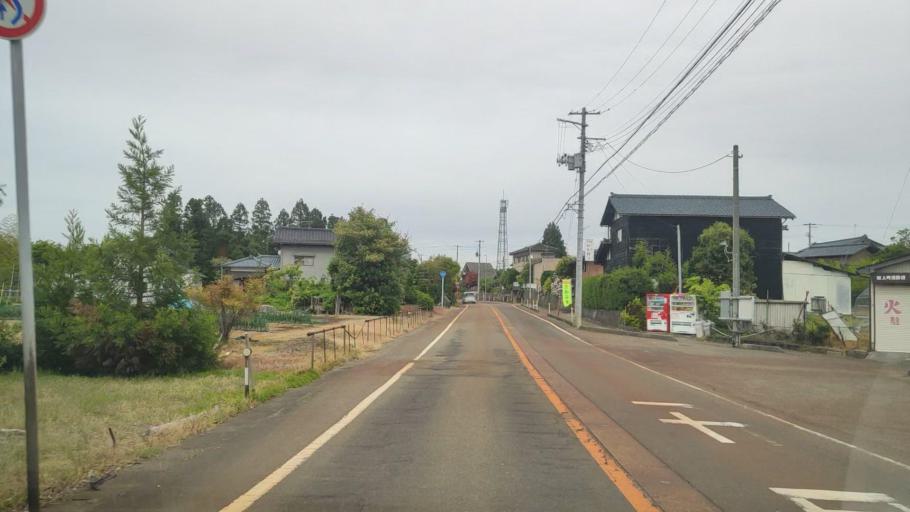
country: JP
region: Niigata
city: Shirone
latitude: 37.7256
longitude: 139.0799
